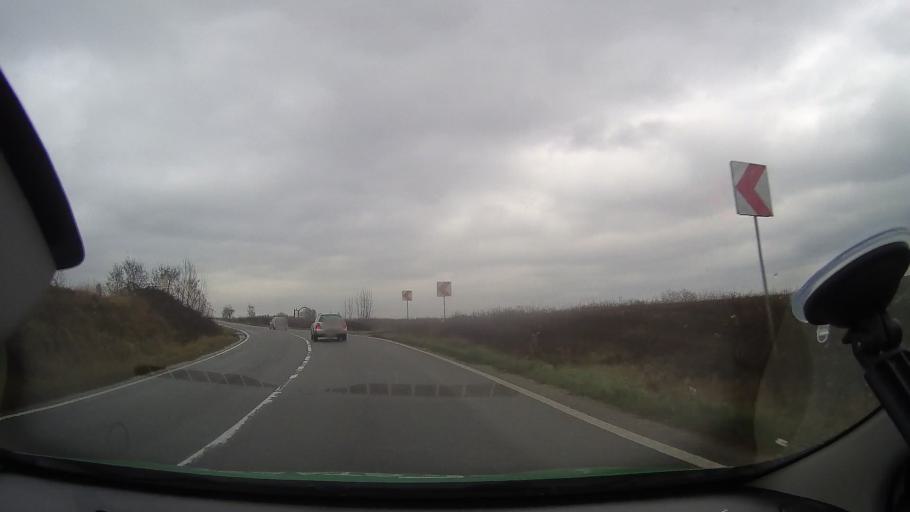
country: RO
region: Arad
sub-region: Comuna Almas
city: Almas
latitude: 46.2825
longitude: 22.2431
